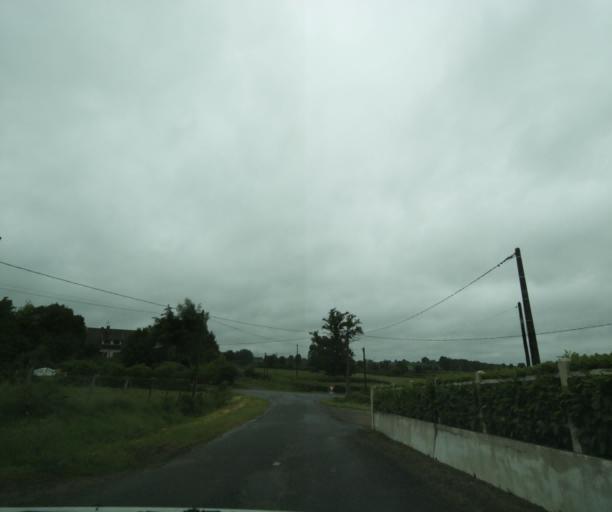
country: FR
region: Bourgogne
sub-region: Departement de Saone-et-Loire
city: Genelard
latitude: 46.5771
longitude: 4.2164
